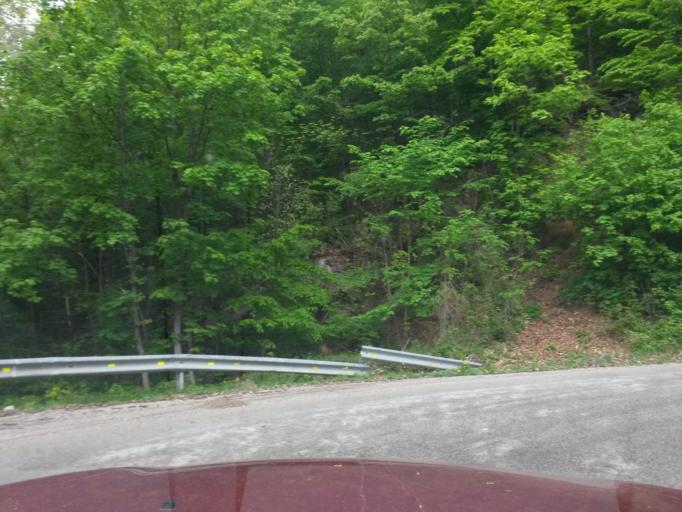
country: SK
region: Kosicky
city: Roznava
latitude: 48.5695
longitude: 20.4715
